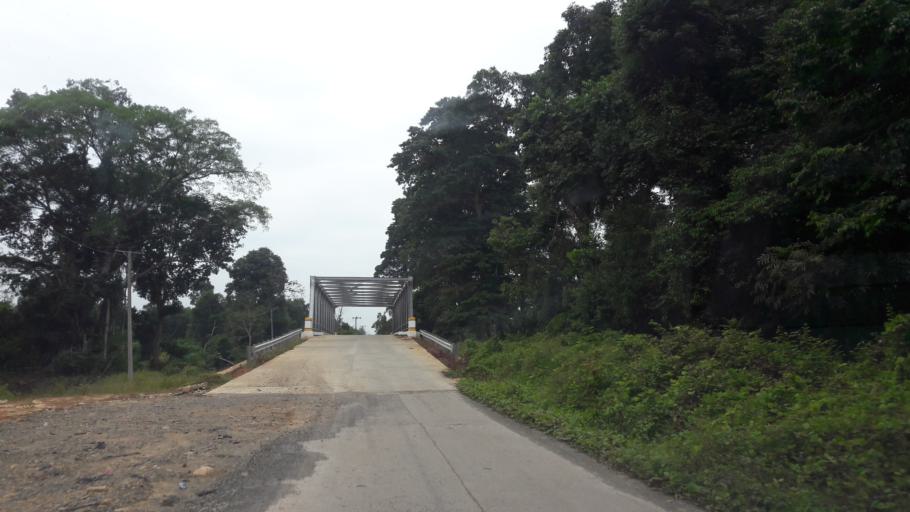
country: ID
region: South Sumatra
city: Gunungmenang
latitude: -3.2042
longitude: 103.9079
